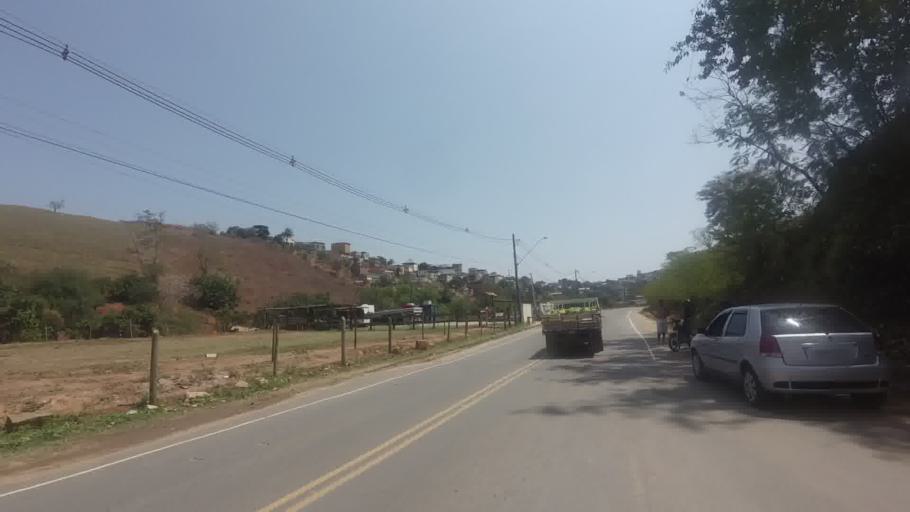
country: BR
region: Espirito Santo
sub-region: Cachoeiro De Itapemirim
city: Cachoeiro de Itapemirim
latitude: -20.8520
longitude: -41.0980
